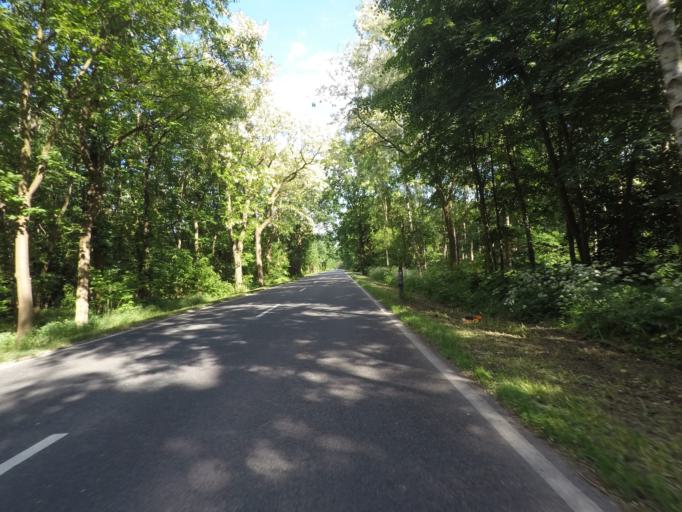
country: DE
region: Brandenburg
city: Britz
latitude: 52.8588
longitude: 13.7923
